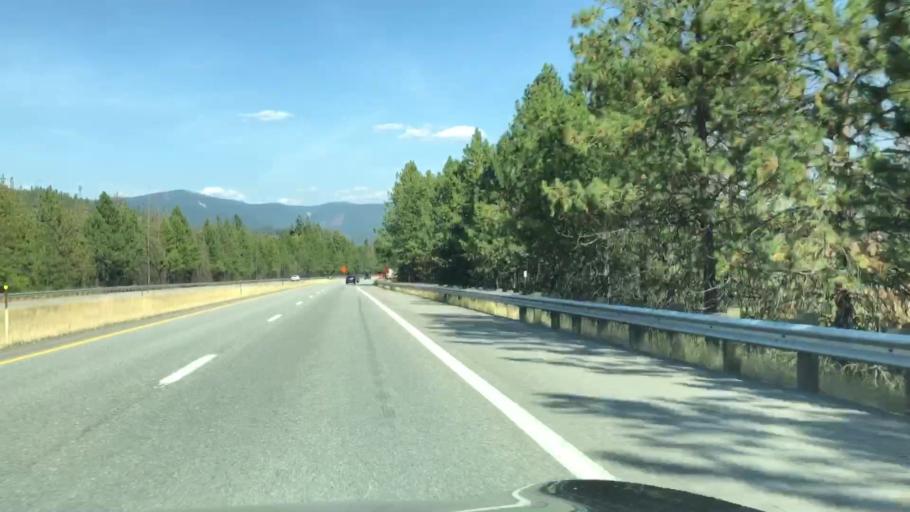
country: US
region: Idaho
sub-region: Shoshone County
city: Pinehurst
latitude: 47.5513
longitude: -116.2907
